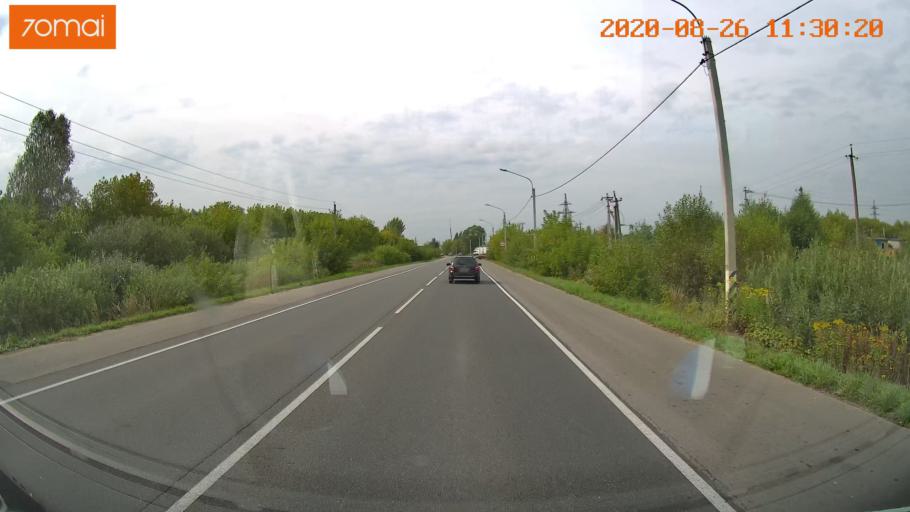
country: RU
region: Rjazan
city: Shilovo
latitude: 54.3157
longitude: 40.8852
